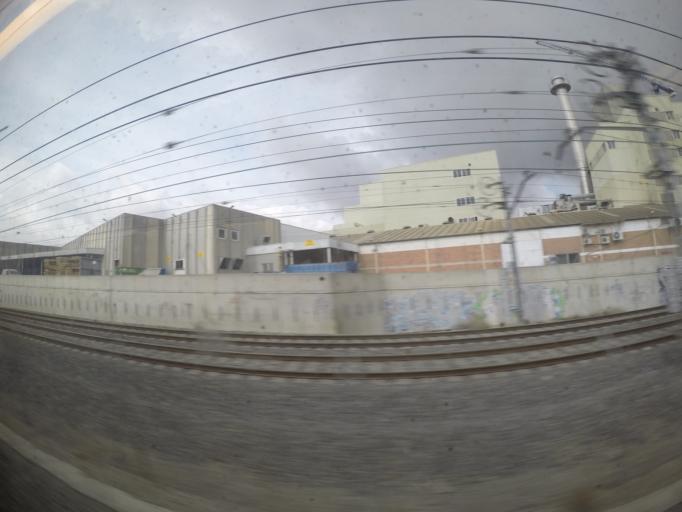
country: ES
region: Catalonia
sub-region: Provincia de Barcelona
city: Castellet
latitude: 41.2901
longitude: 1.6195
